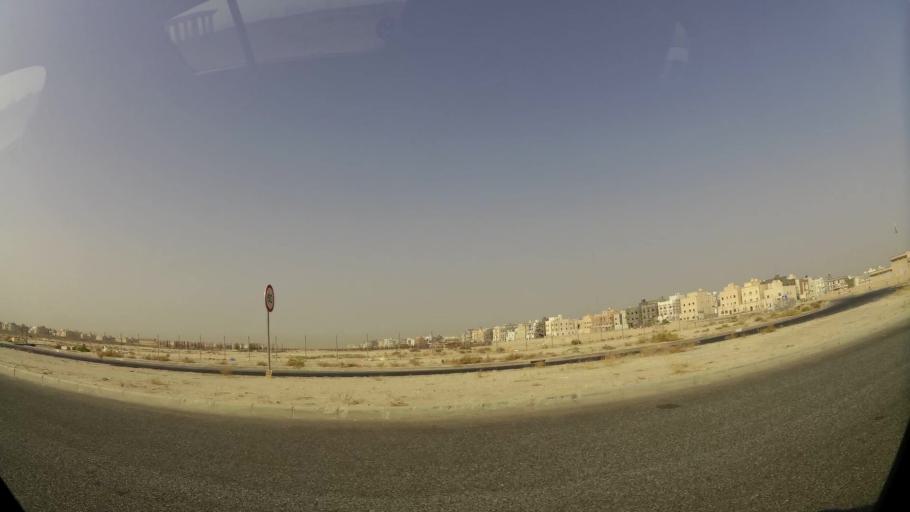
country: KW
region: Muhafazat al Jahra'
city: Al Jahra'
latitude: 29.3466
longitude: 47.7810
